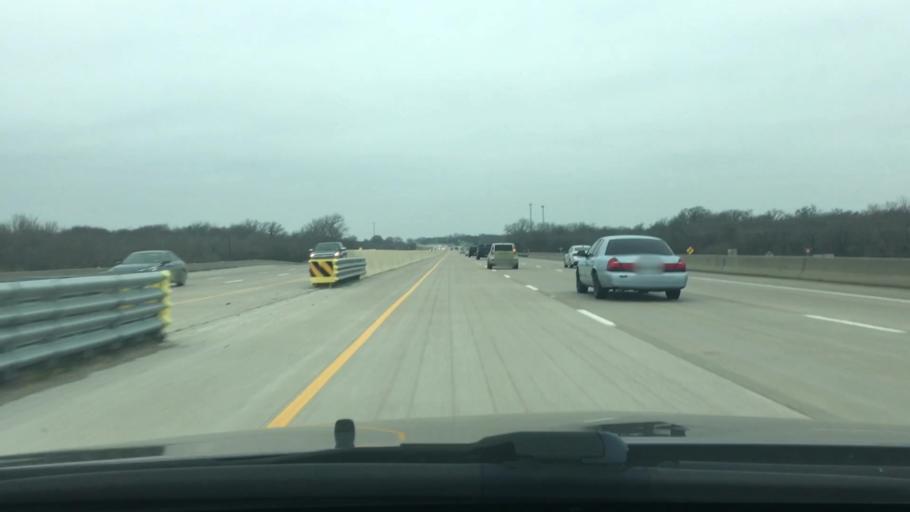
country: US
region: Texas
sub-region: Navarro County
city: Corsicana
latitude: 31.9470
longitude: -96.4226
